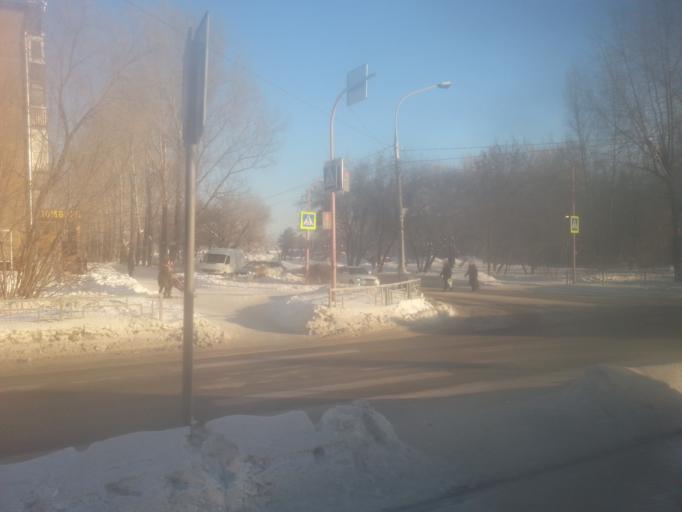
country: RU
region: Altai Krai
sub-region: Gorod Barnaulskiy
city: Barnaul
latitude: 53.3574
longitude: 83.7088
